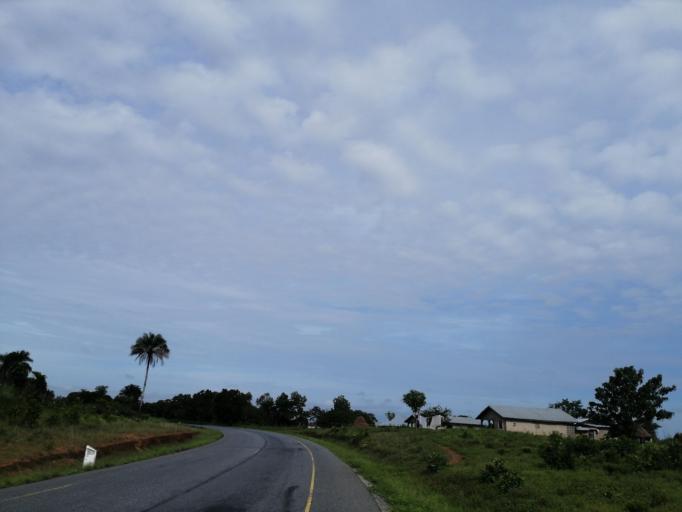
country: SL
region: Northern Province
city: Port Loko
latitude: 8.7732
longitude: -12.8650
